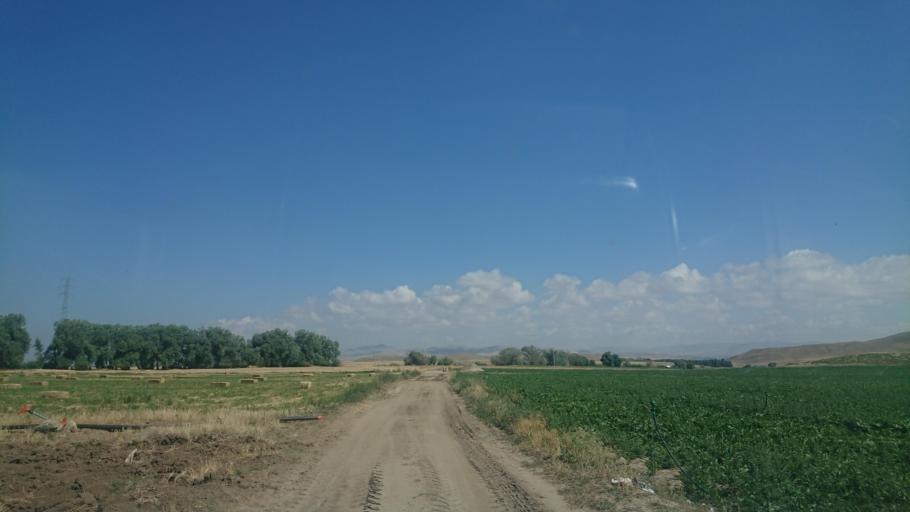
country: TR
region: Aksaray
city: Sariyahsi
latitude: 38.9951
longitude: 33.8952
